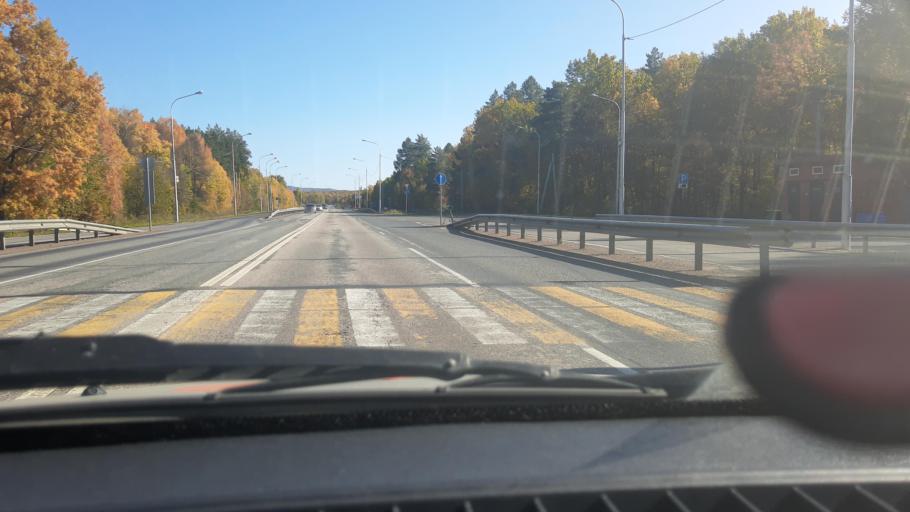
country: RU
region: Bashkortostan
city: Kudeyevskiy
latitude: 54.3953
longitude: 56.8111
